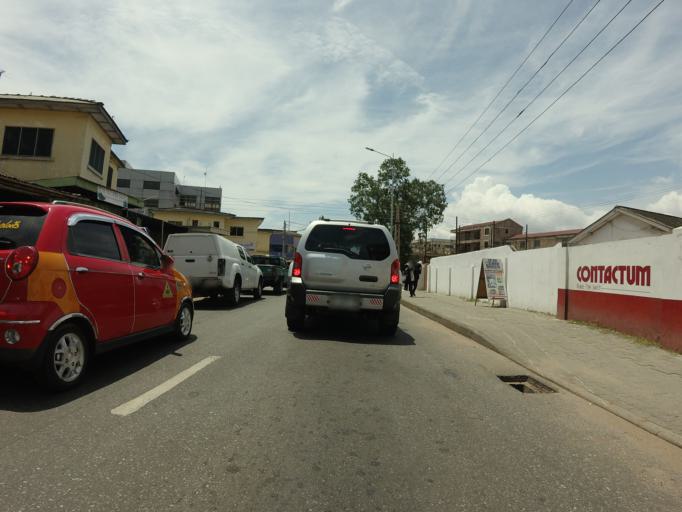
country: GH
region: Greater Accra
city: Accra
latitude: 5.5563
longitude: -0.2103
